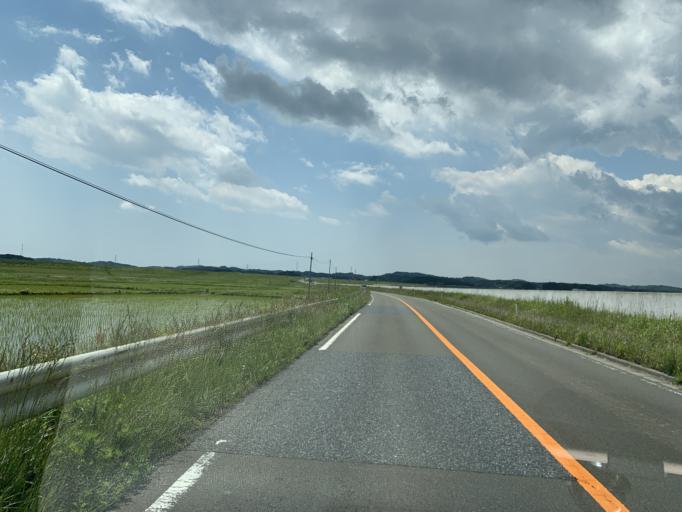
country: JP
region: Miyagi
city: Matsushima
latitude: 38.4473
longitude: 141.0808
